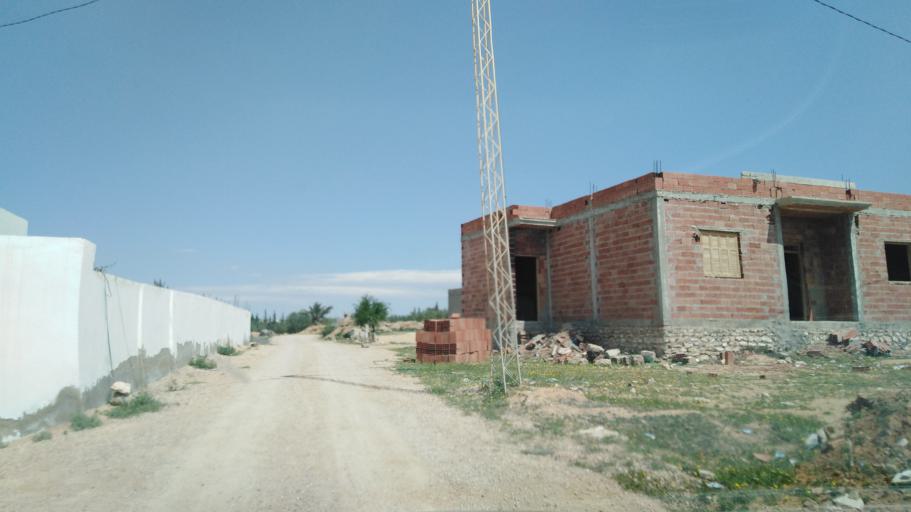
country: TN
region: Safaqis
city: Sfax
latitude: 34.7624
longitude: 10.5244
